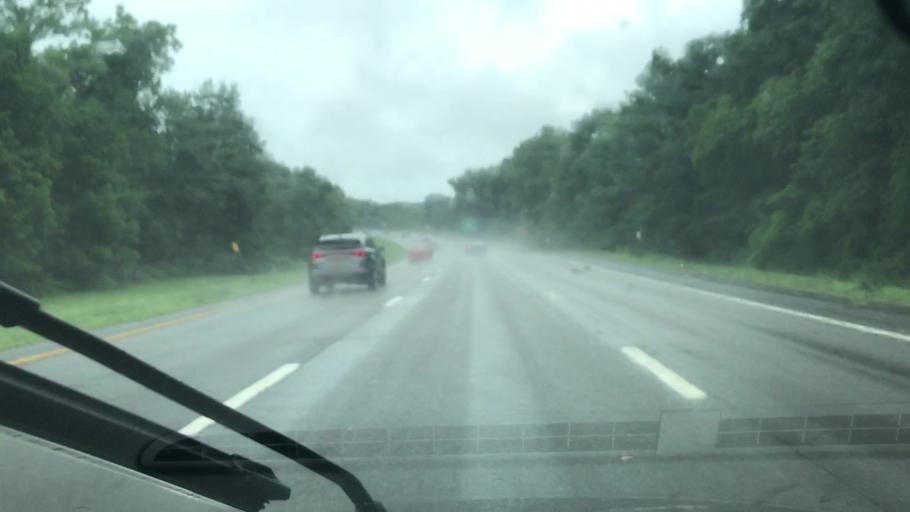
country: US
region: New York
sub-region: Westchester County
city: Briarcliff Manor
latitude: 41.2101
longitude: -73.8093
